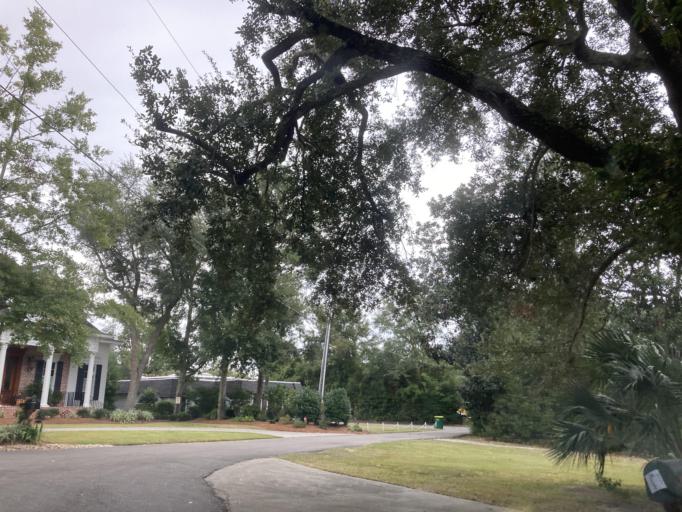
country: US
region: Mississippi
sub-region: Jackson County
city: Gulf Hills
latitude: 30.4281
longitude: -88.8395
